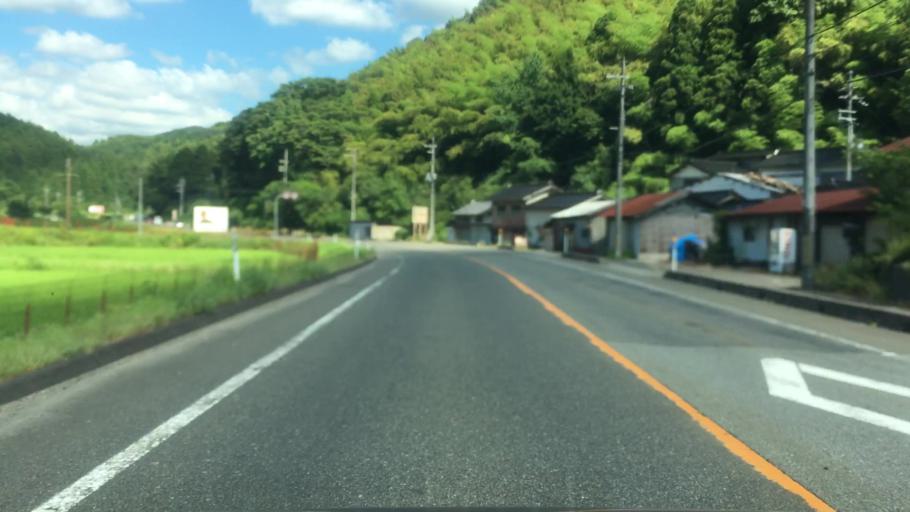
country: JP
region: Hyogo
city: Toyooka
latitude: 35.5712
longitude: 134.7795
